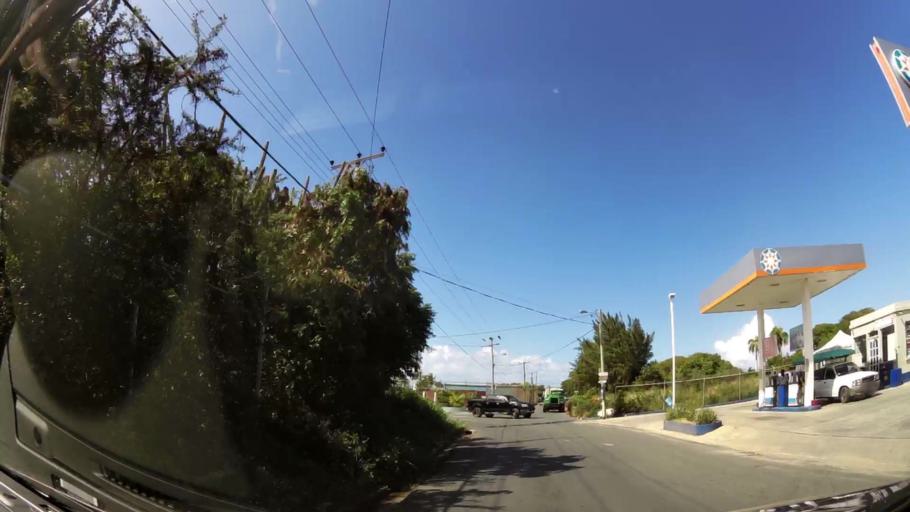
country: VG
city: Tortola
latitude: 18.4528
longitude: -64.4348
